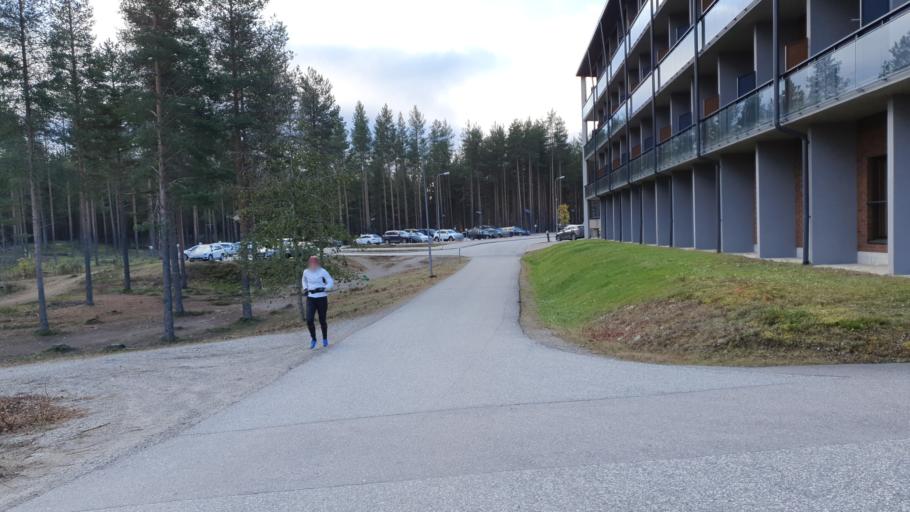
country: FI
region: Kainuu
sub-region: Kajaani
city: Vuokatti
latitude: 64.1416
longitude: 28.2958
